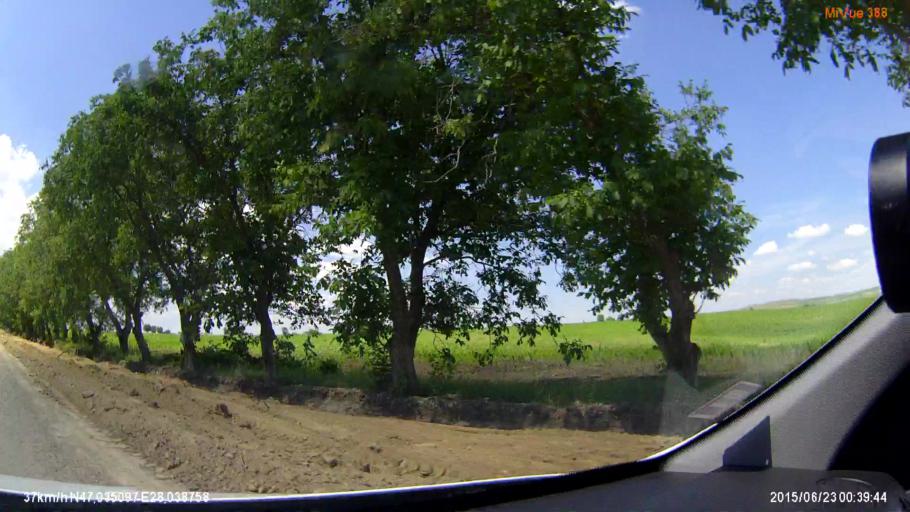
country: RO
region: Iasi
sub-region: Comuna Grozesti
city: Grozesti
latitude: 47.0351
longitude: 28.0389
